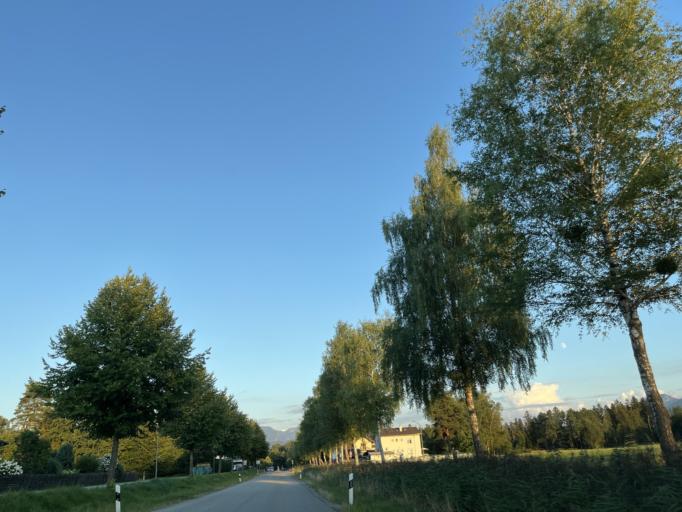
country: DE
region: Bavaria
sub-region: Upper Bavaria
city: Raubling
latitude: 47.7903
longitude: 12.0771
